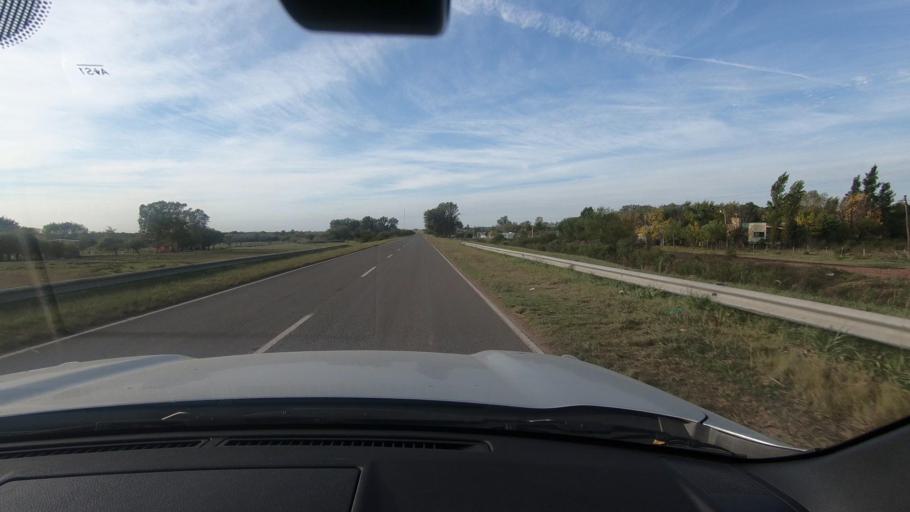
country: AR
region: Entre Rios
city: Colon
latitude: -32.2533
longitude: -58.2150
